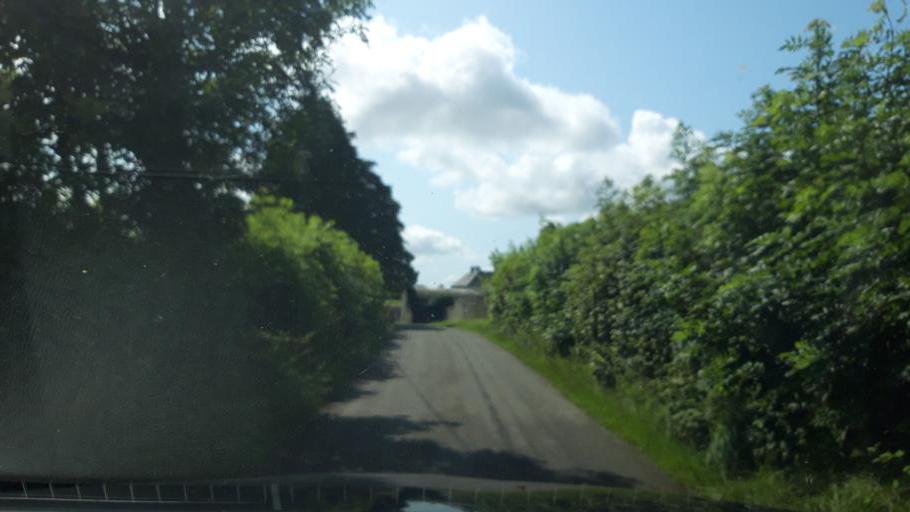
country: IE
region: Leinster
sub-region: Kilkenny
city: Graiguenamanagh
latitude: 52.5698
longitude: -6.9806
